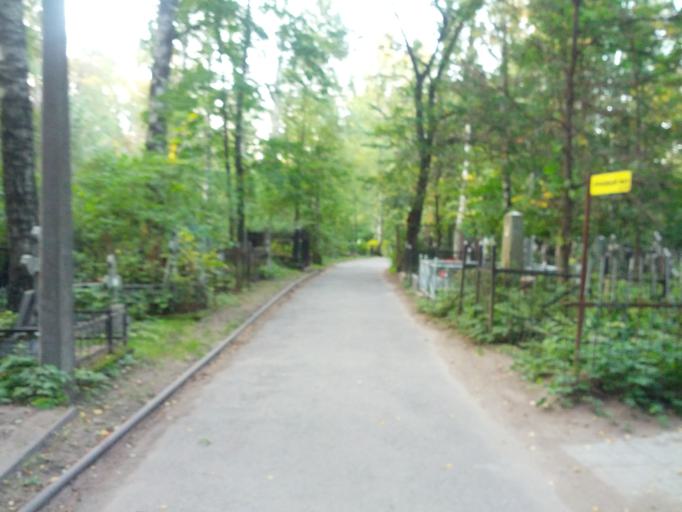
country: RU
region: St.-Petersburg
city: Krasnogvargeisky
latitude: 59.9472
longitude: 30.4287
